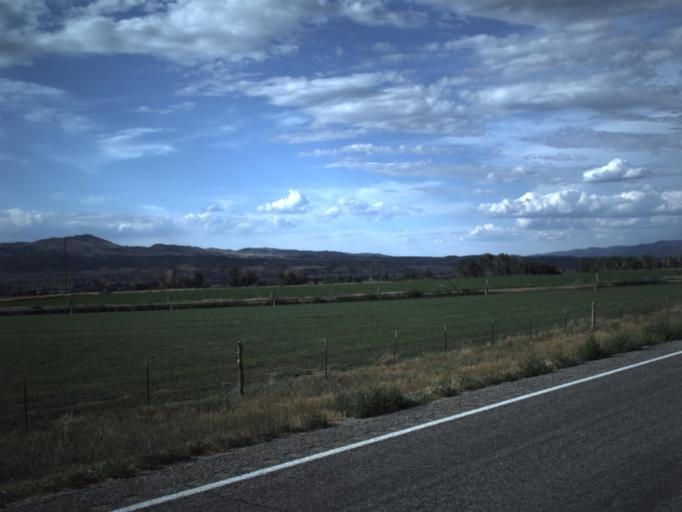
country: US
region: Utah
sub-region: Sanpete County
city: Mount Pleasant
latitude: 39.5113
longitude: -111.4950
